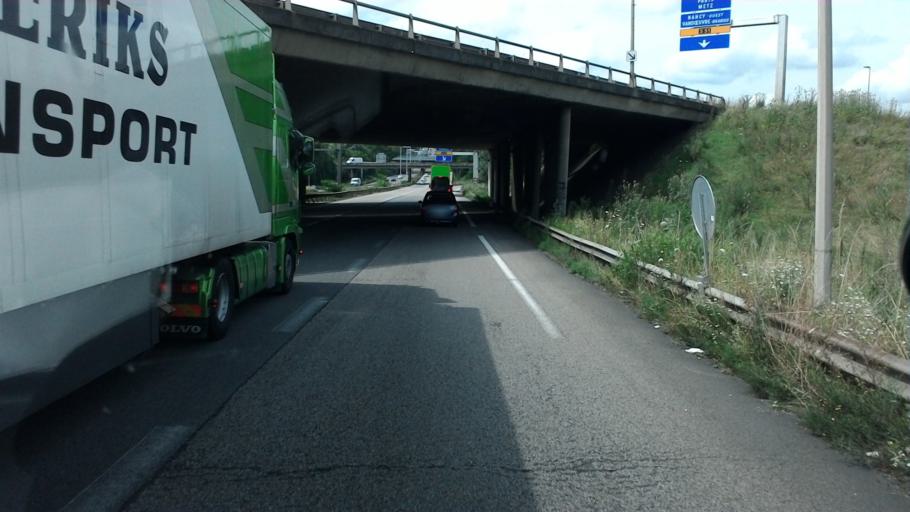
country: FR
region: Lorraine
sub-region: Departement de Meurthe-et-Moselle
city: Fleville-devant-Nancy
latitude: 48.6261
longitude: 6.1843
